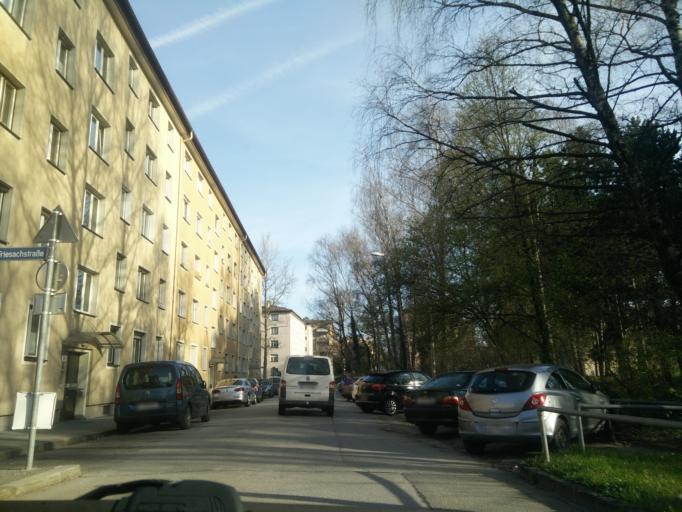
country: AT
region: Salzburg
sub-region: Politischer Bezirk Salzburg-Umgebung
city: Bergheim
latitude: 47.8148
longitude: 13.0332
